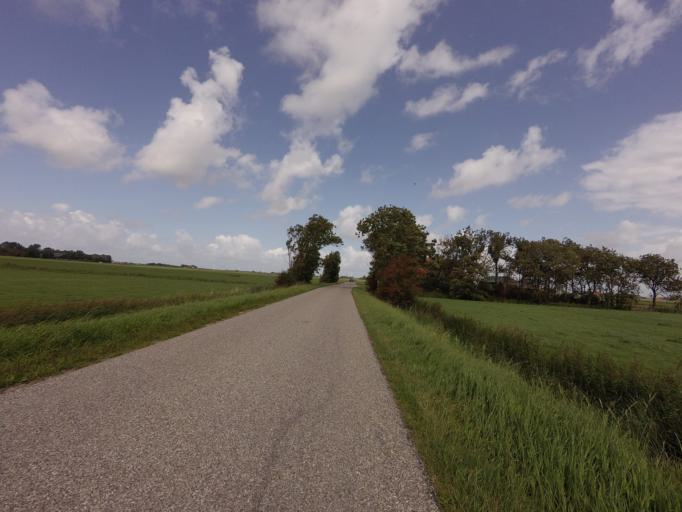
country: NL
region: Friesland
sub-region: Gemeente Franekeradeel
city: Sexbierum
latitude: 53.1601
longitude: 5.4833
